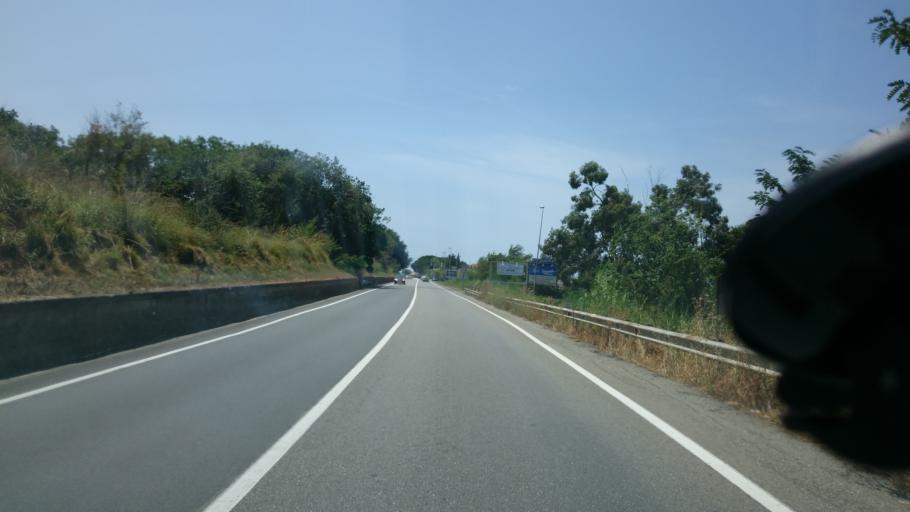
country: IT
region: Calabria
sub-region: Provincia di Cosenza
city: Cittadella del Capo
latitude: 39.5832
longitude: 15.8699
